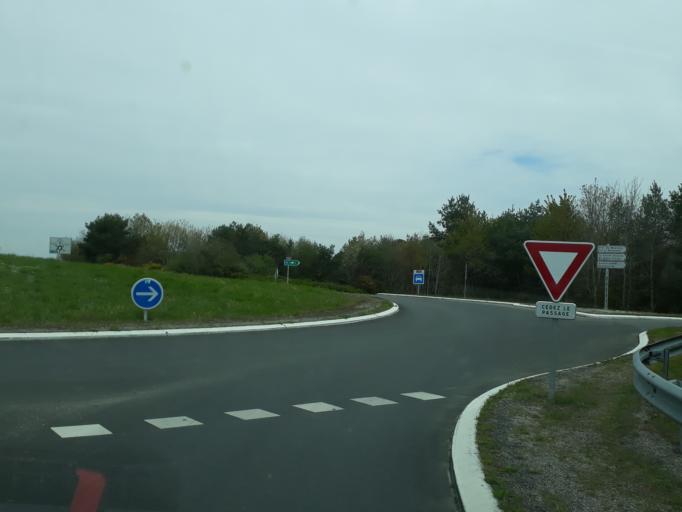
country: FR
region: Brittany
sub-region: Departement du Morbihan
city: Surzur
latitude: 47.6100
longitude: -2.6139
